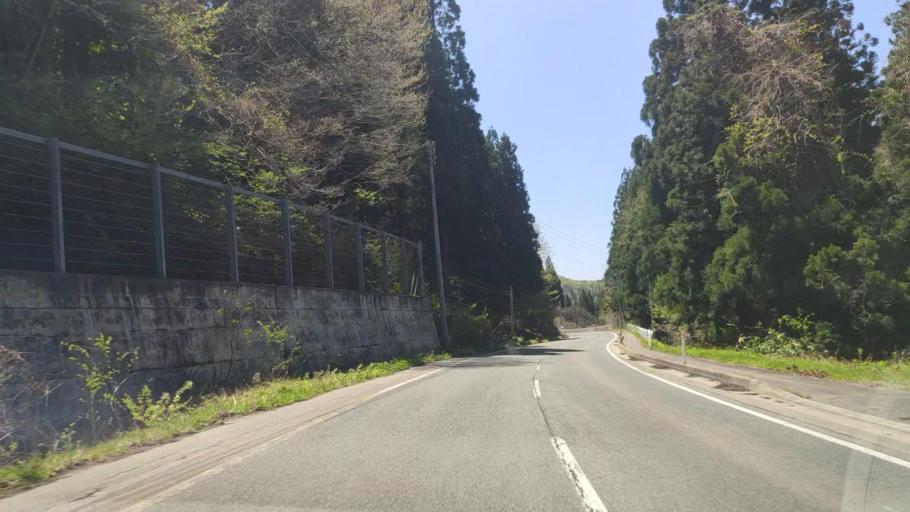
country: JP
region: Yamagata
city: Shinjo
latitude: 38.8969
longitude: 140.3273
